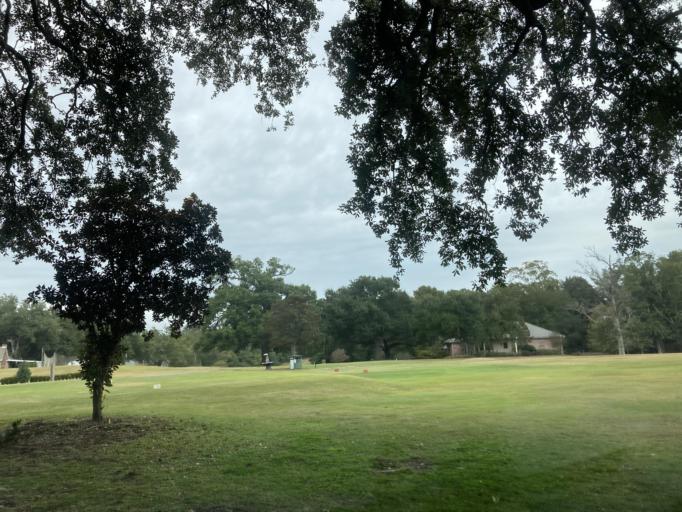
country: US
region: Mississippi
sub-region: Jackson County
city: Gulf Hills
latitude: 30.4264
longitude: -88.8371
